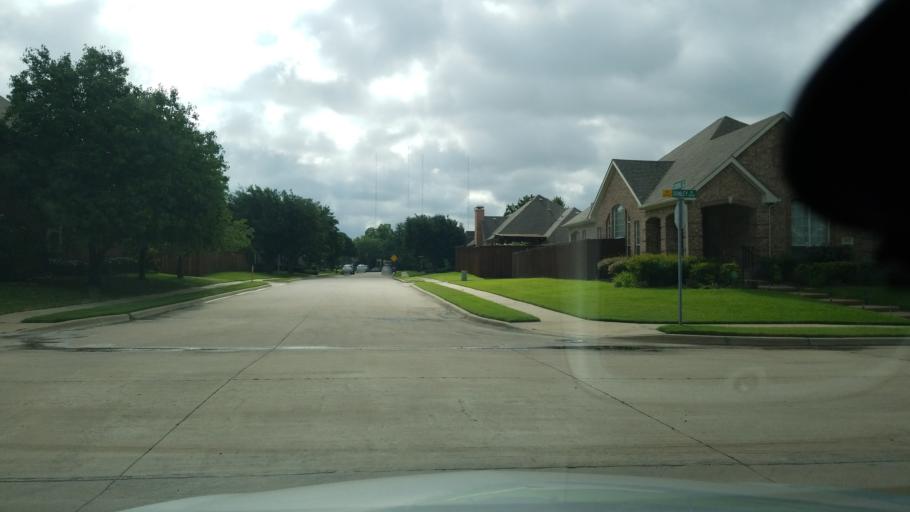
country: US
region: Texas
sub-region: Dallas County
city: Farmers Branch
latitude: 32.9450
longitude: -96.9496
